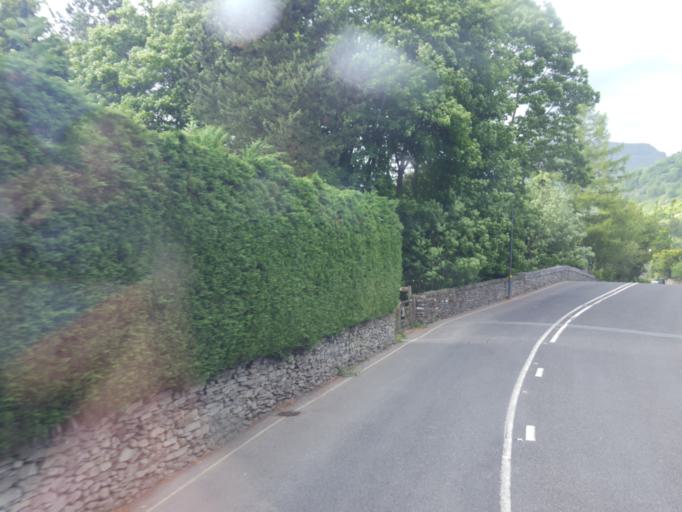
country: GB
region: England
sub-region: Cumbria
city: Ambleside
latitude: 54.4629
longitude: -3.0227
